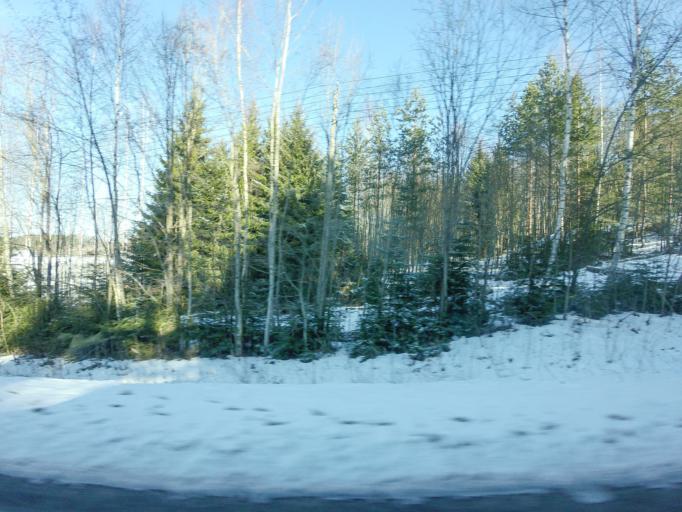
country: FI
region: Uusimaa
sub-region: Raaseporin
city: Inga
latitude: 60.0921
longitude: 23.9298
